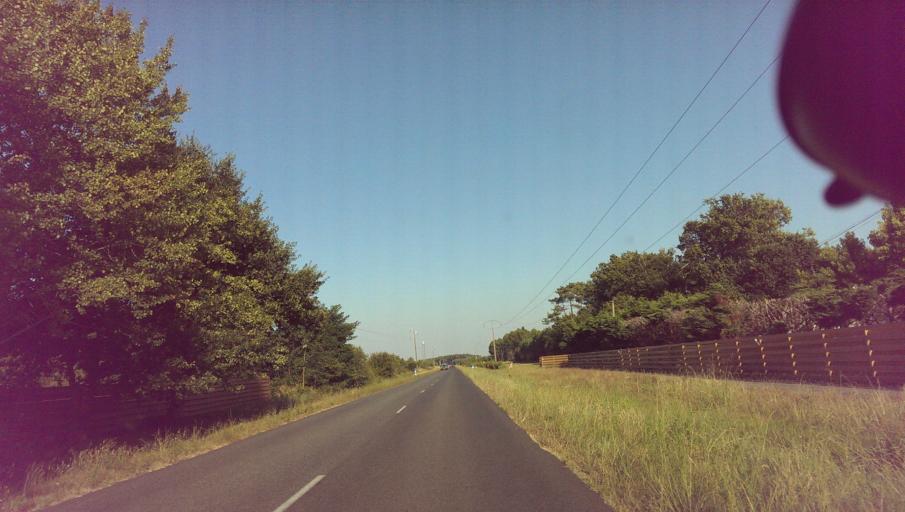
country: FR
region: Aquitaine
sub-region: Departement des Landes
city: Mimizan
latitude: 44.1824
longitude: -1.1813
